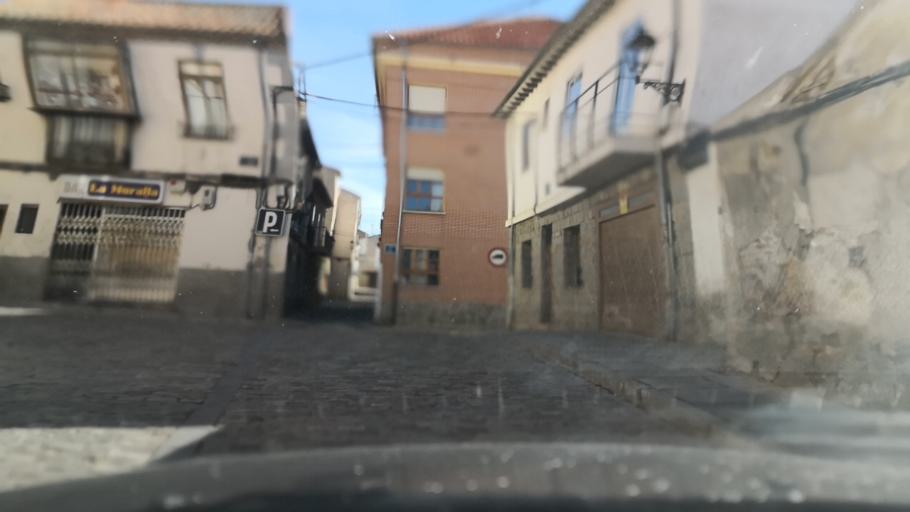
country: ES
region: Castille and Leon
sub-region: Provincia de Avila
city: Avila
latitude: 40.6521
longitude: -4.7018
